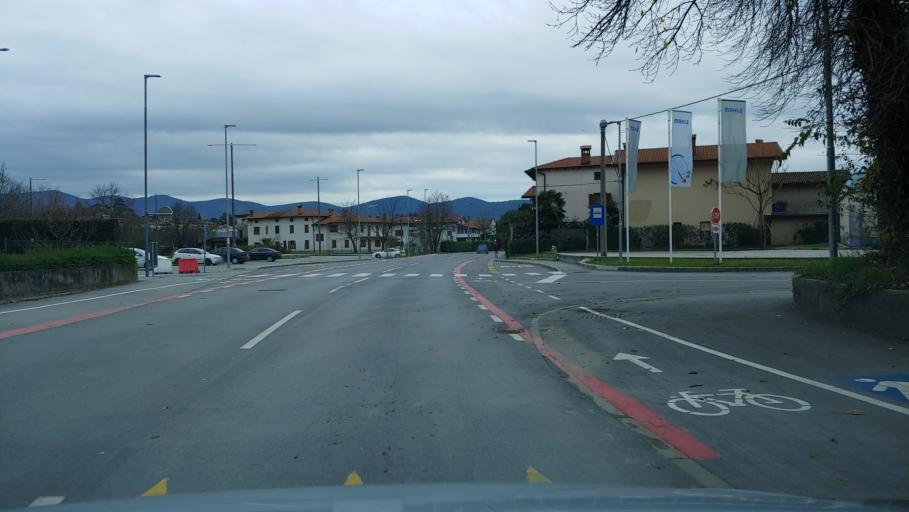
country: SI
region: Sempeter-Vrtojba
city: Sempeter pri Gorici
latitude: 45.9246
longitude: 13.6407
